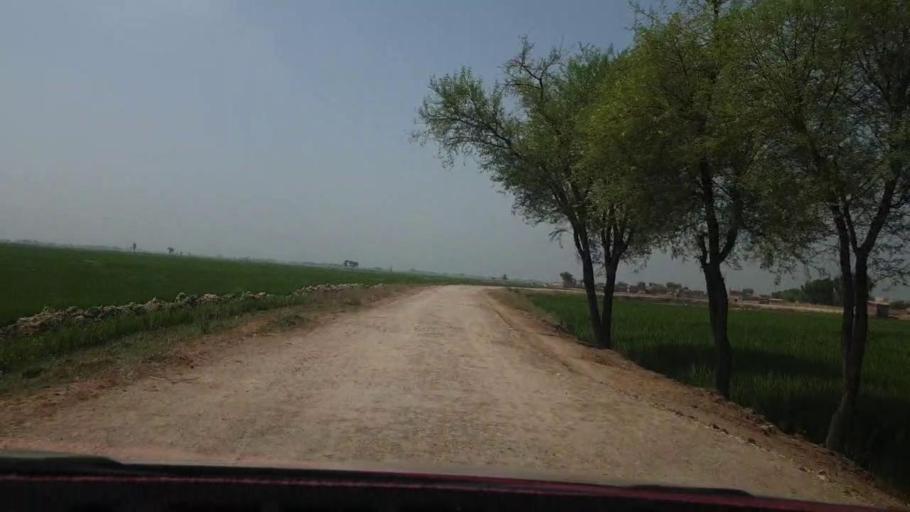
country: PK
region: Sindh
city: Nasirabad
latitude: 27.3974
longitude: 67.8498
